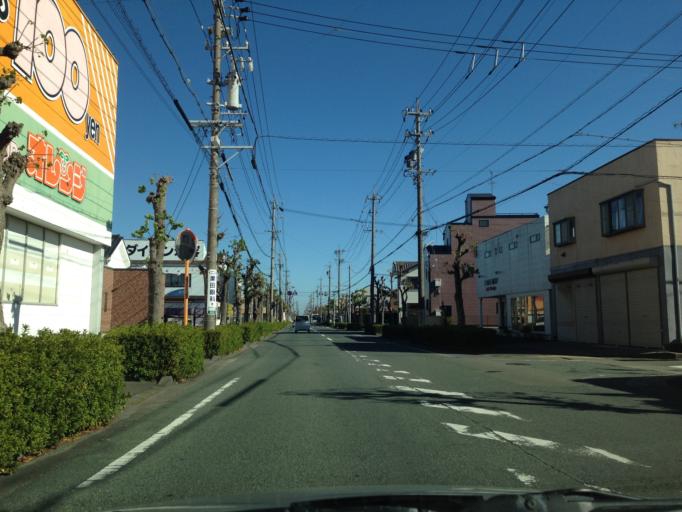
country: JP
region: Shizuoka
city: Fukuroi
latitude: 34.7474
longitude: 137.9275
